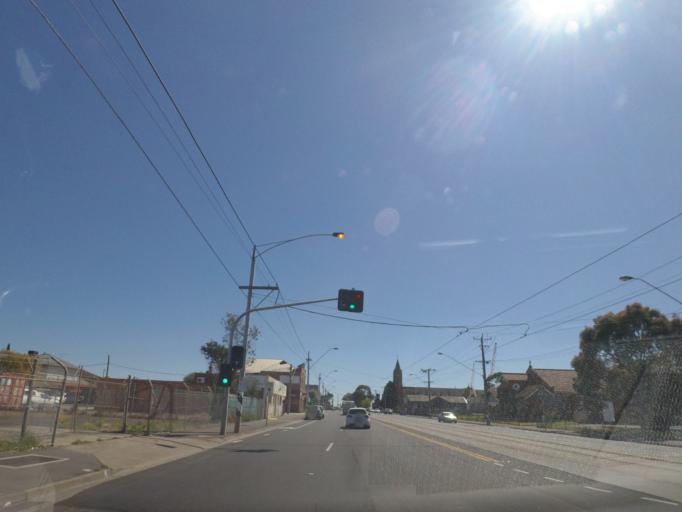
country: AU
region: Victoria
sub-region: Moreland
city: Coburg
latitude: -37.7402
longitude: 144.9667
